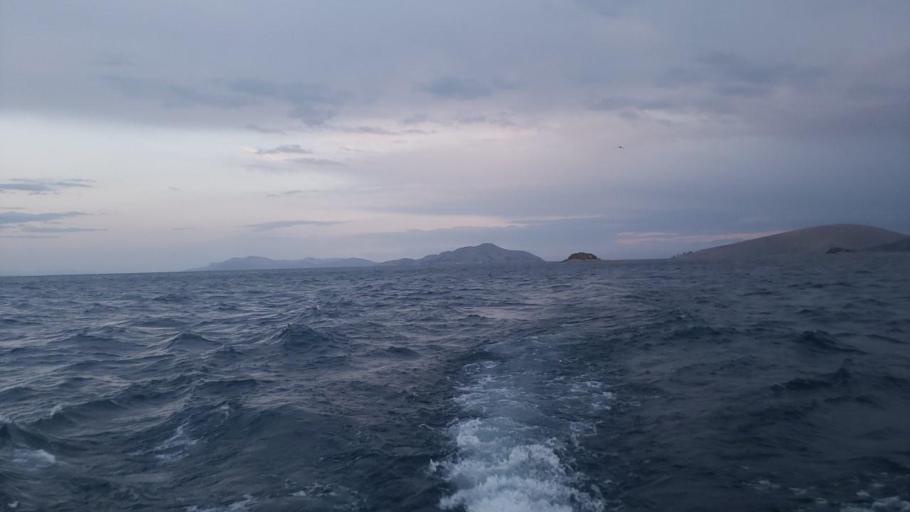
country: BO
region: La Paz
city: San Pablo
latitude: -16.2347
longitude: -68.8307
